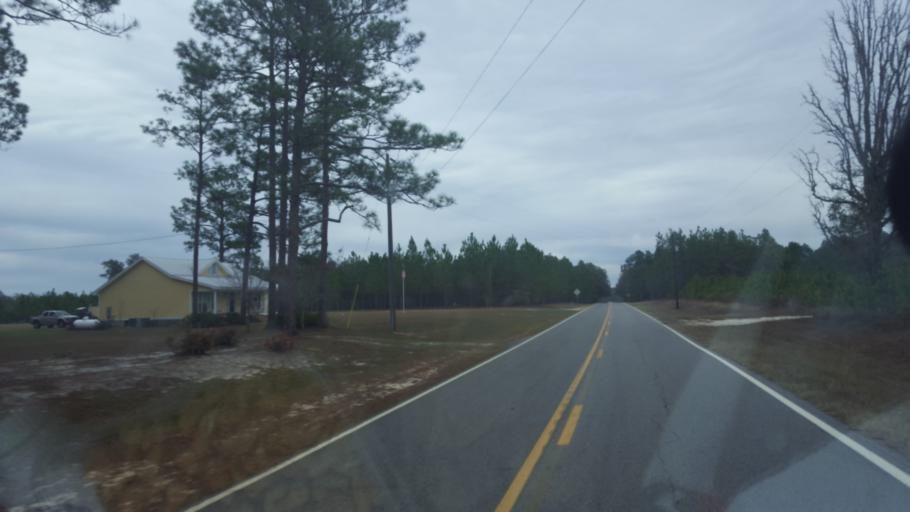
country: US
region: Georgia
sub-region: Wilcox County
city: Rochelle
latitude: 31.8087
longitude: -83.4606
